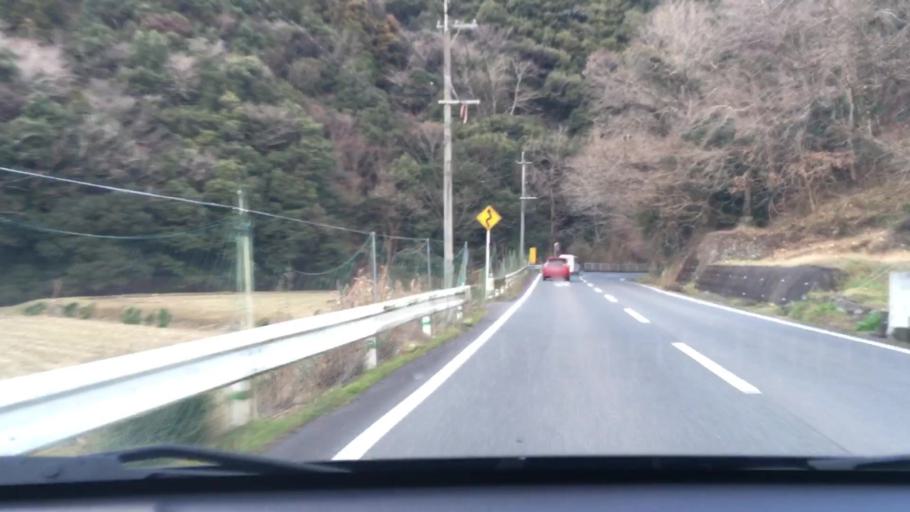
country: JP
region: Oita
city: Bungo-Takada-shi
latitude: 33.4618
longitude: 131.3892
